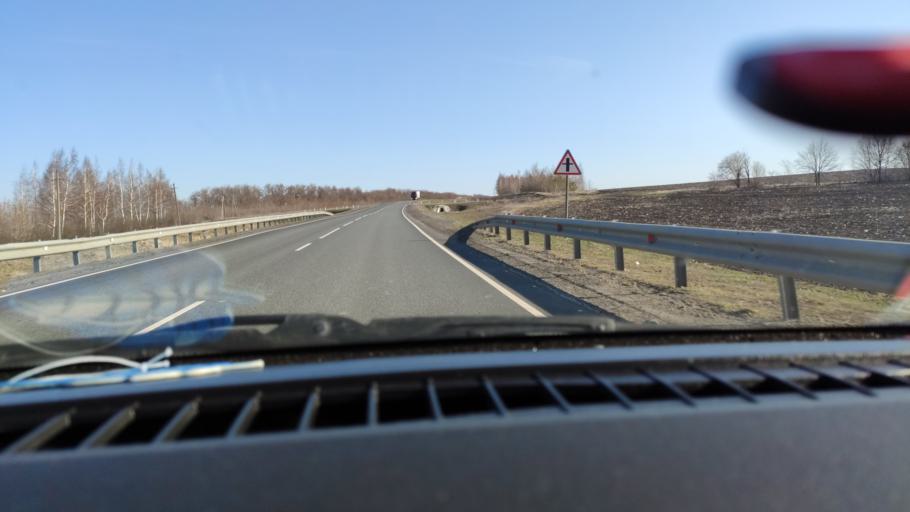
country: RU
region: Samara
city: Syzran'
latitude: 52.9752
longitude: 48.3094
